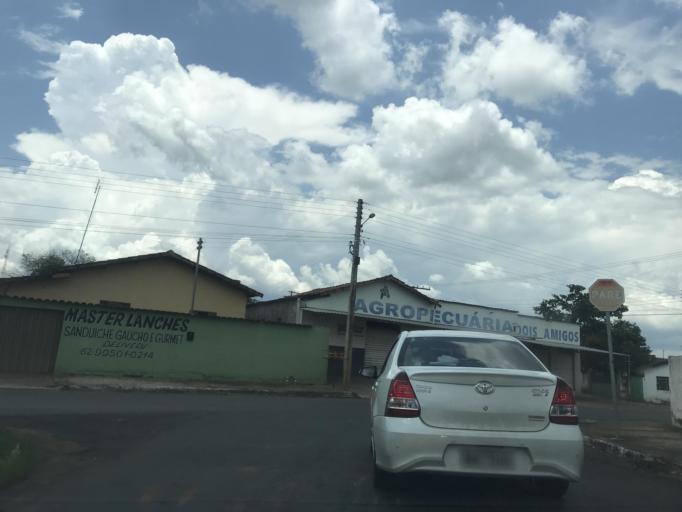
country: BR
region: Goias
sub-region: Bela Vista De Goias
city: Bela Vista de Goias
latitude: -17.0596
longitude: -48.6643
